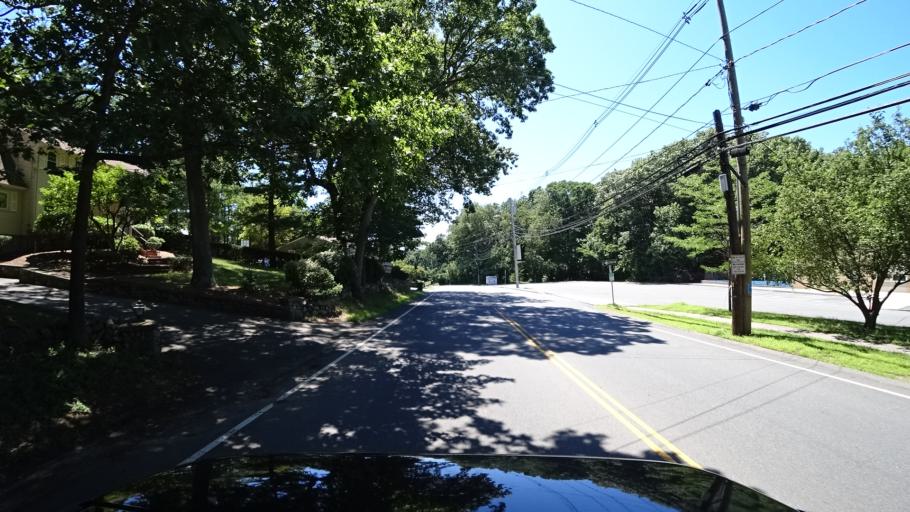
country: US
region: Massachusetts
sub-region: Norfolk County
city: Dedham
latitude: 42.2244
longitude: -71.1553
